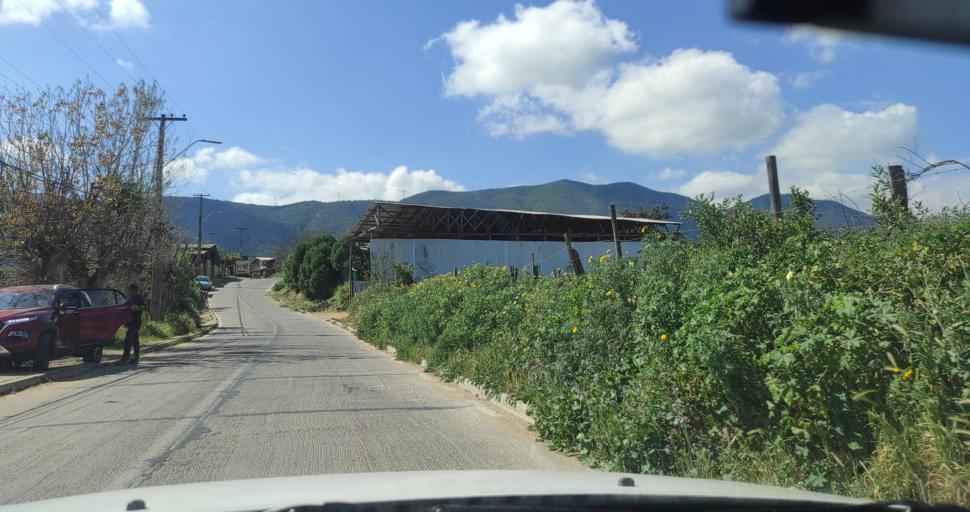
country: CL
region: Valparaiso
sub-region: Provincia de Marga Marga
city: Limache
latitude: -32.9948
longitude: -71.2260
